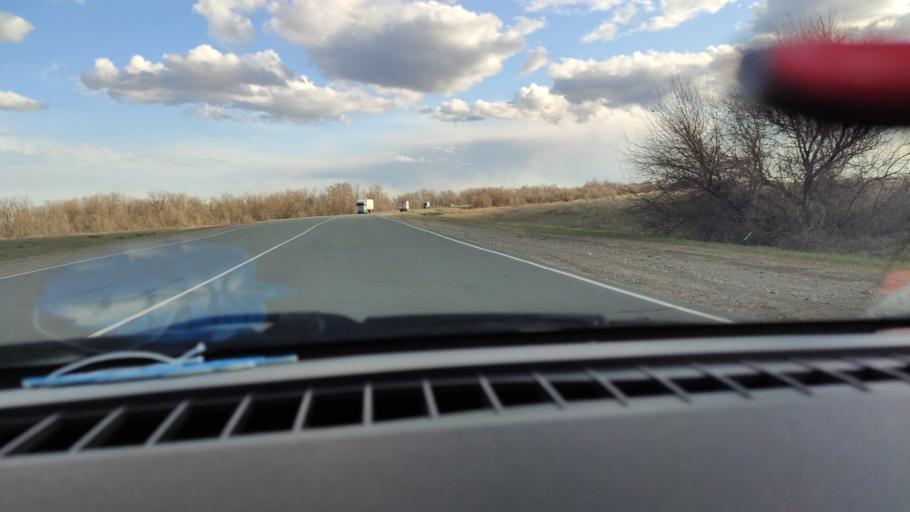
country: RU
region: Saratov
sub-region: Saratovskiy Rayon
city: Saratov
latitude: 51.7142
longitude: 46.0237
